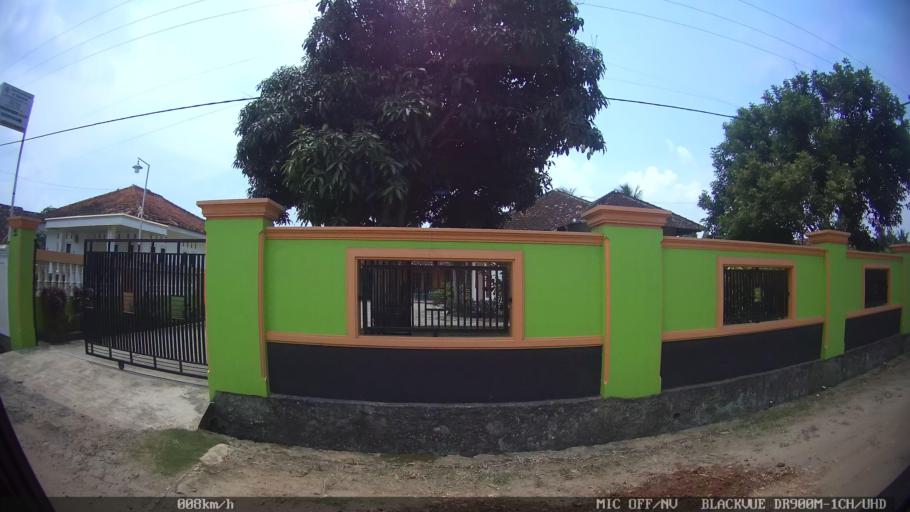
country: ID
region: Lampung
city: Natar
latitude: -5.3127
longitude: 105.2213
